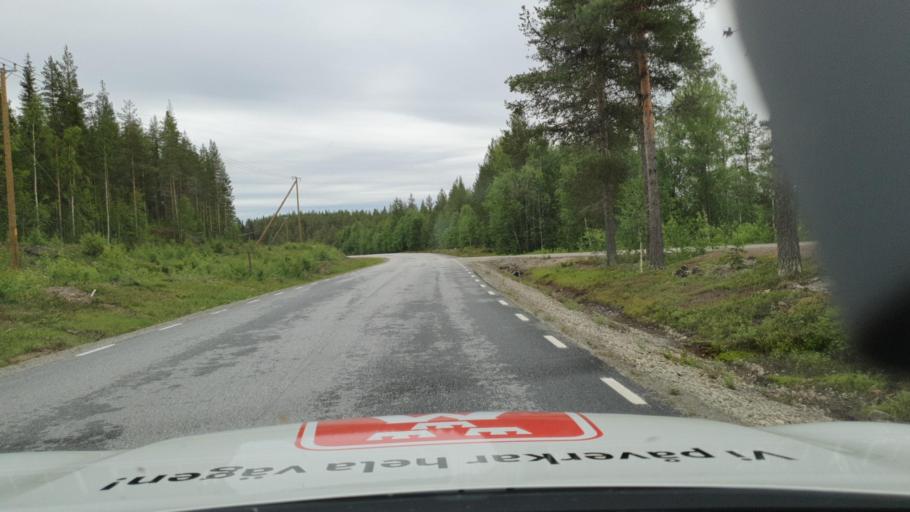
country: SE
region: Vaesterbotten
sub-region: Lycksele Kommun
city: Lycksele
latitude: 64.0955
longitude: 18.3696
